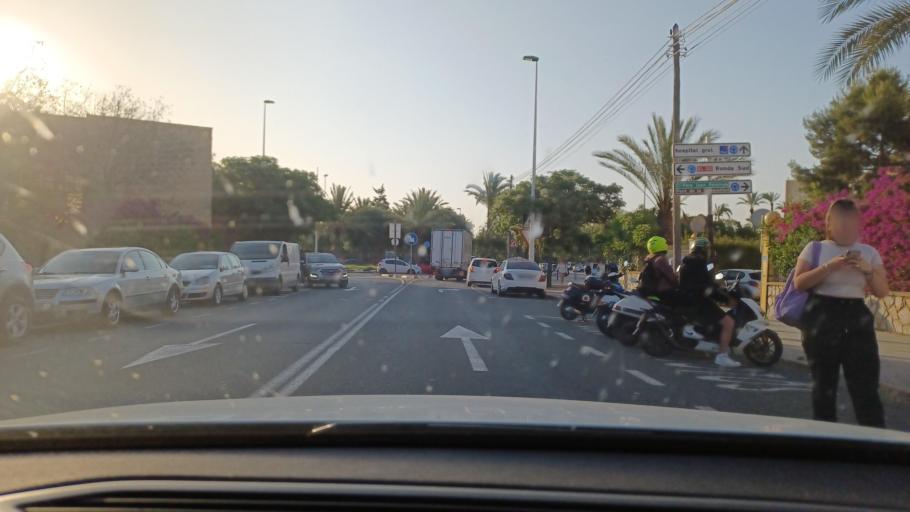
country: ES
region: Valencia
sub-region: Provincia de Alicante
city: Elche
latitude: 38.2621
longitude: -0.6867
